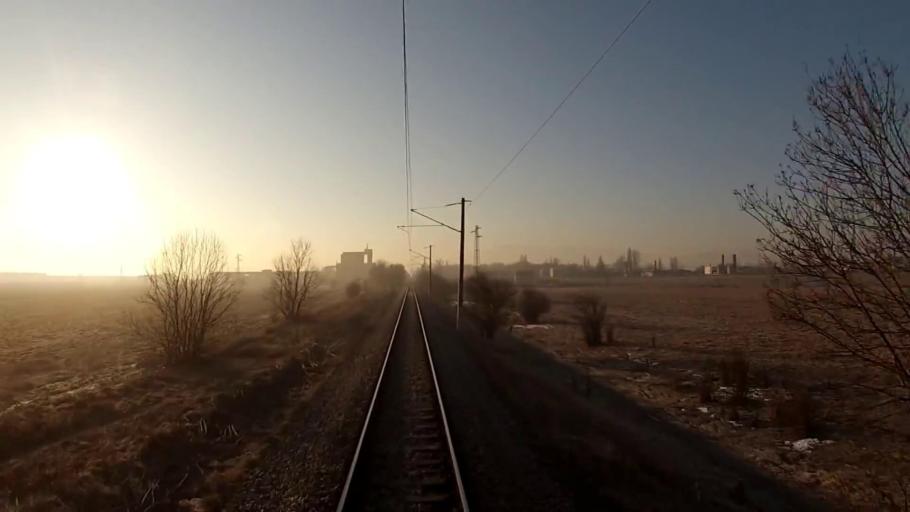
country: BG
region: Sofiya
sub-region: Obshtina Kostinbrod
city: Kostinbrod
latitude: 42.7927
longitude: 23.2094
